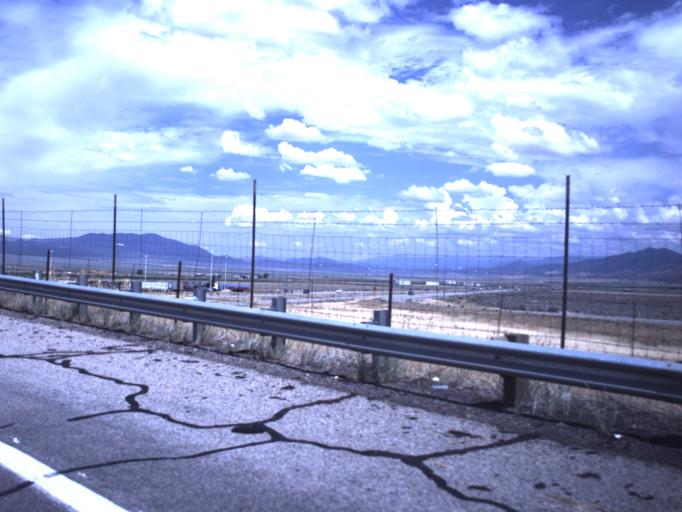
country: US
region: Utah
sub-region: Iron County
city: Parowan
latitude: 37.8576
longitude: -112.8279
